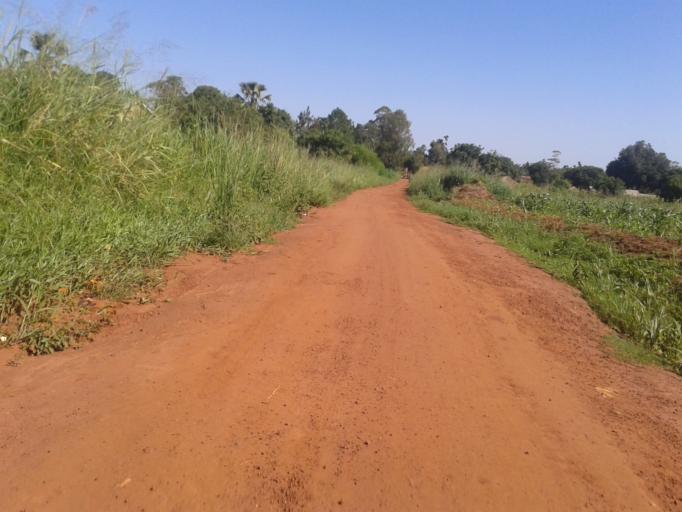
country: UG
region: Northern Region
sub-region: Gulu District
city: Gulu
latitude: 2.7884
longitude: 32.3078
